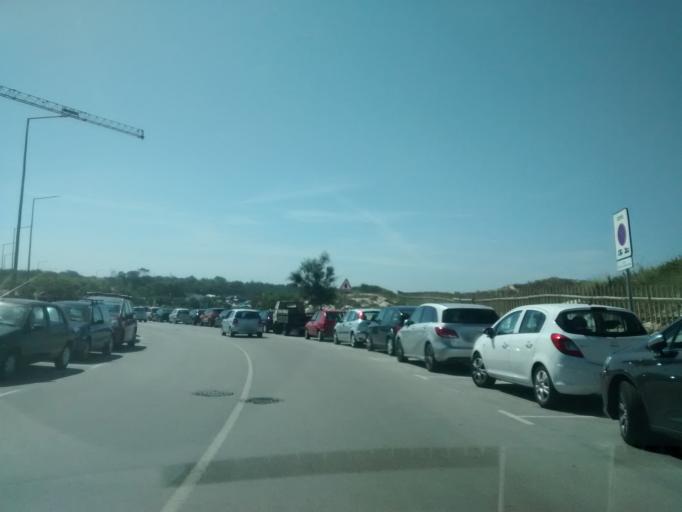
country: PT
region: Coimbra
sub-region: Mira
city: Mira
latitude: 40.4520
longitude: -8.8037
